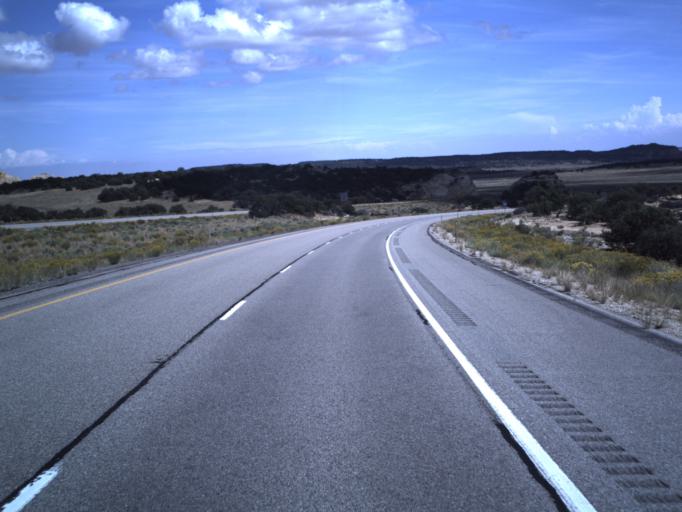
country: US
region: Utah
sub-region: Emery County
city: Ferron
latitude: 38.8661
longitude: -110.8053
